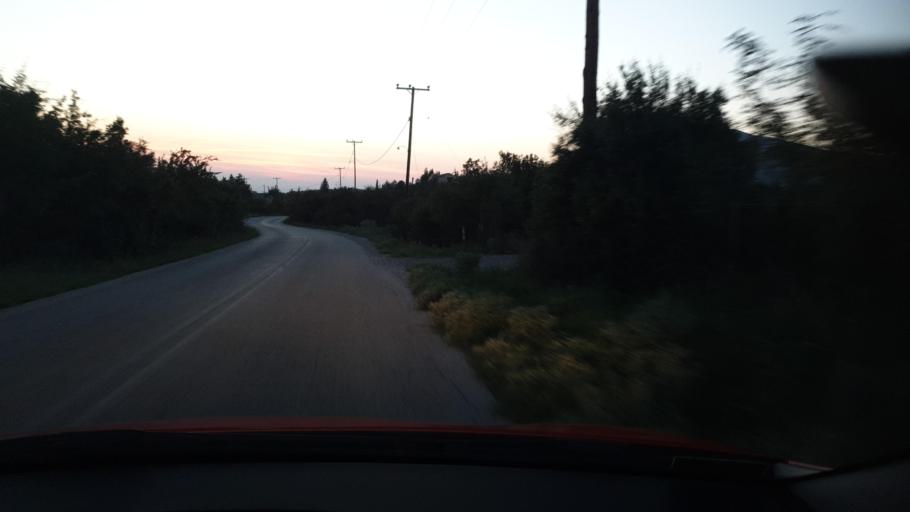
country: GR
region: Central Macedonia
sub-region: Nomos Thessalonikis
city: Vasilika
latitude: 40.5089
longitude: 23.1414
